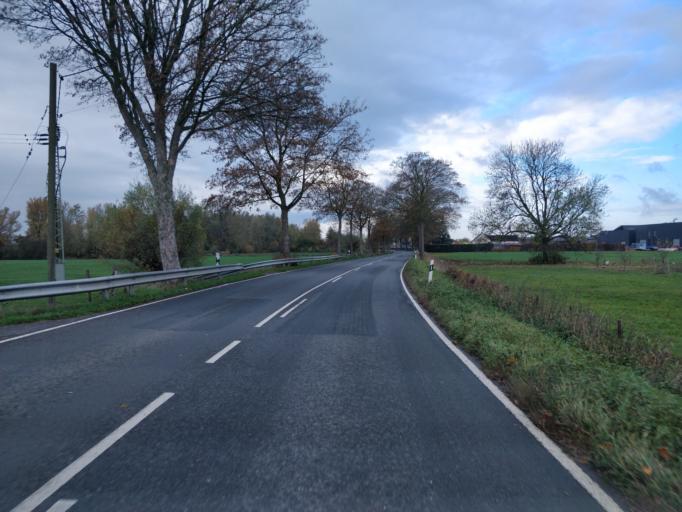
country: DE
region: North Rhine-Westphalia
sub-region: Regierungsbezirk Dusseldorf
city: Emmerich
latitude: 51.8435
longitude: 6.2879
